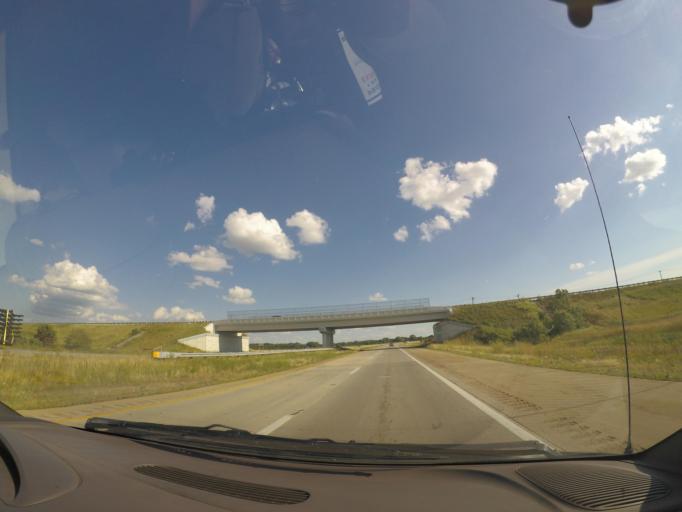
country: US
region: Ohio
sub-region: Lucas County
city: Whitehouse
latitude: 41.4746
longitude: -83.7766
